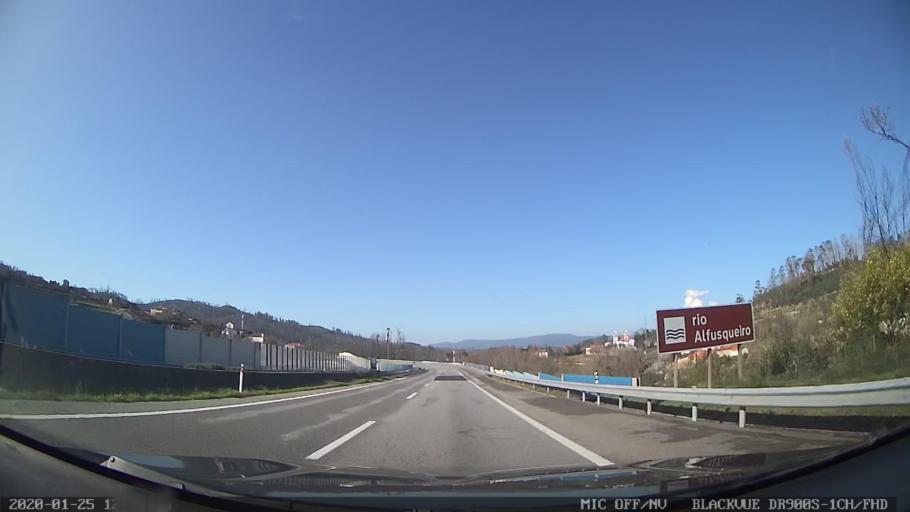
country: PT
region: Viseu
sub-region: Vouzela
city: Vouzela
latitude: 40.6837
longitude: -8.1488
